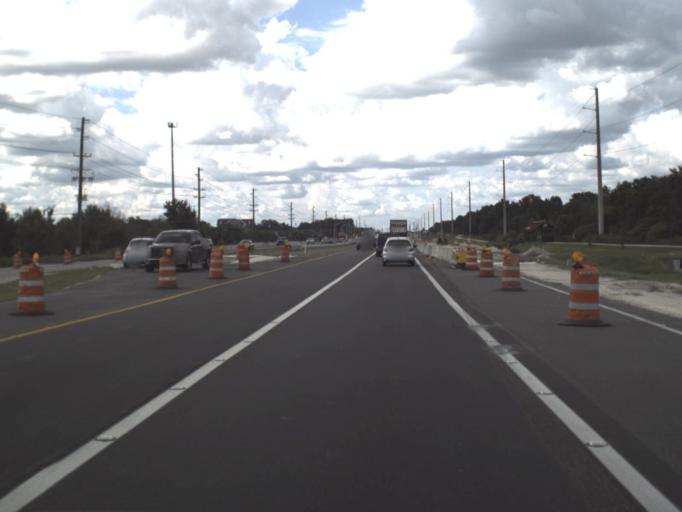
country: US
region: Florida
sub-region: Polk County
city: Highland City
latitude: 27.9829
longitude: -81.8899
